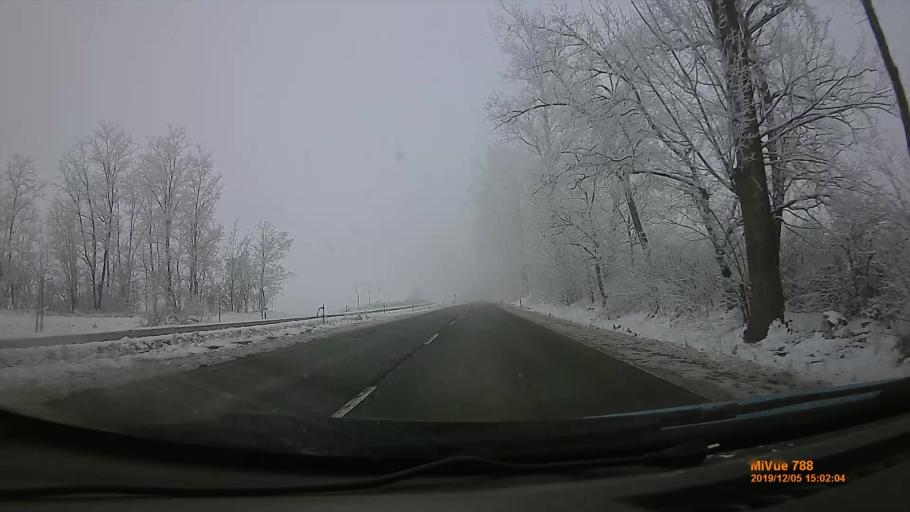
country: HU
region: Szabolcs-Szatmar-Bereg
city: Tiszanagyfalu
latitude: 48.0726
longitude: 21.5195
